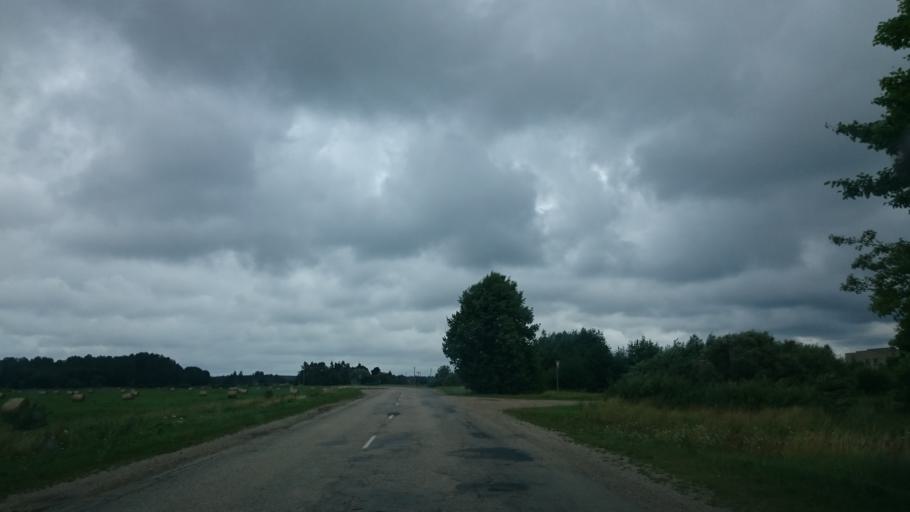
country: LV
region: Pavilostas
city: Pavilosta
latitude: 56.8655
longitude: 21.2251
